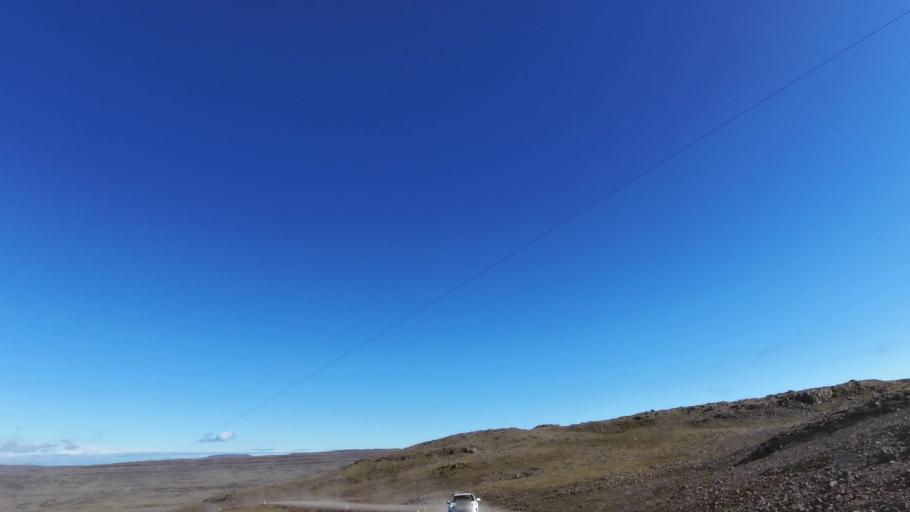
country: IS
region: West
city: Olafsvik
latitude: 65.5547
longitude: -24.2290
